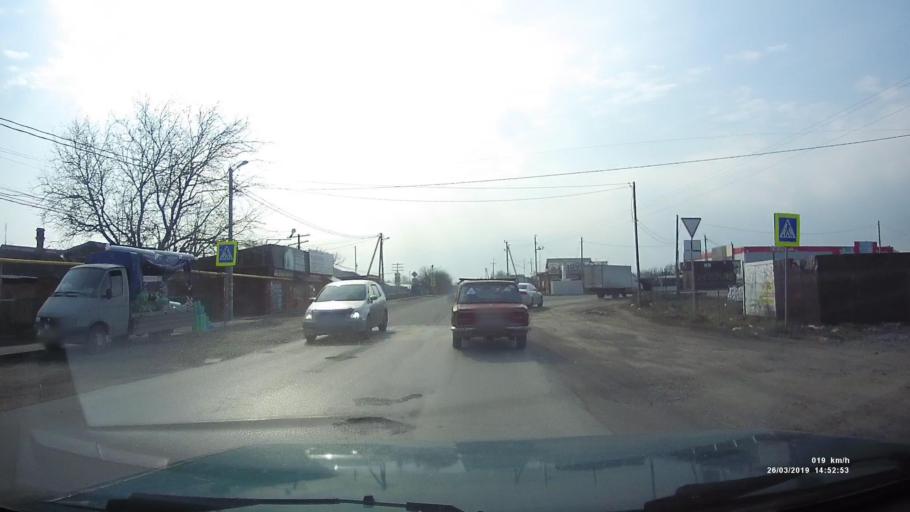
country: RU
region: Rostov
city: Novobessergenovka
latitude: 47.1825
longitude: 38.8204
